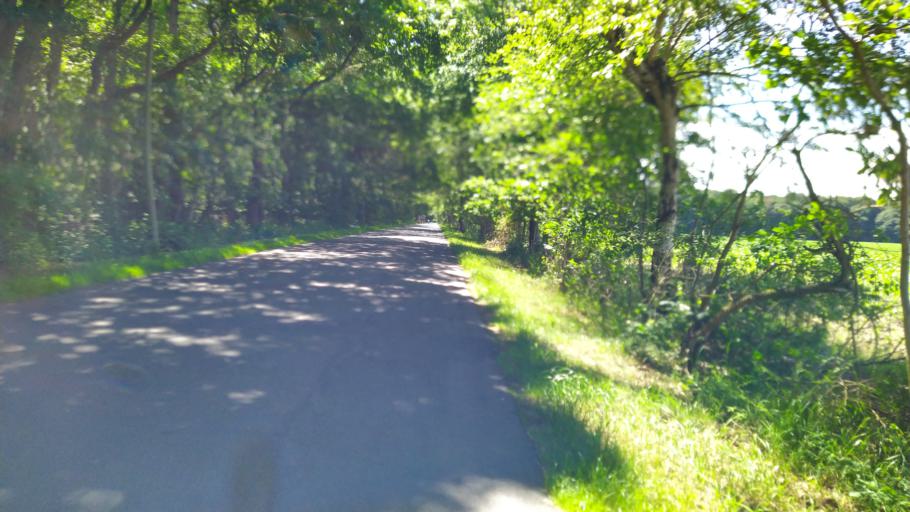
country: DE
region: Lower Saxony
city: Oldendorf
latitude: 53.5600
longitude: 9.2366
